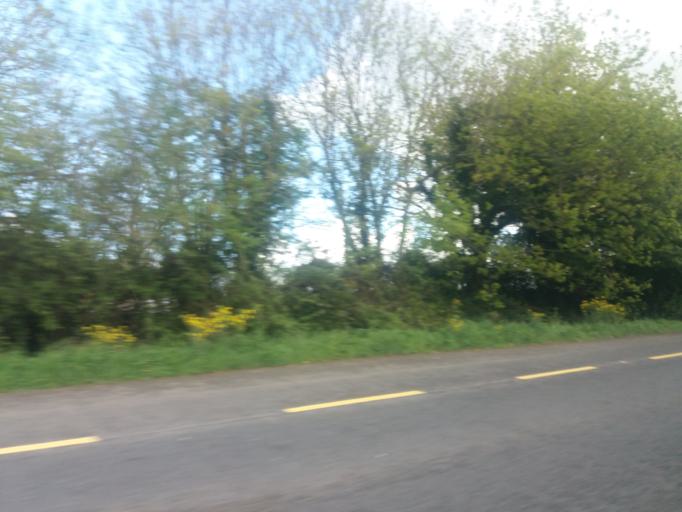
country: IE
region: Leinster
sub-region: Loch Garman
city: Ferns
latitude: 52.5808
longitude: -6.5143
